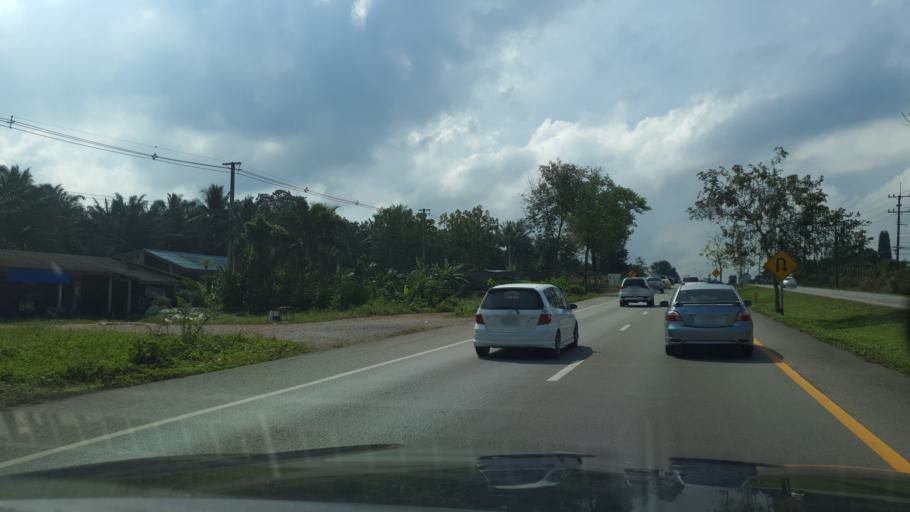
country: TH
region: Chumphon
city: Pathio
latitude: 10.8270
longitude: 99.2139
